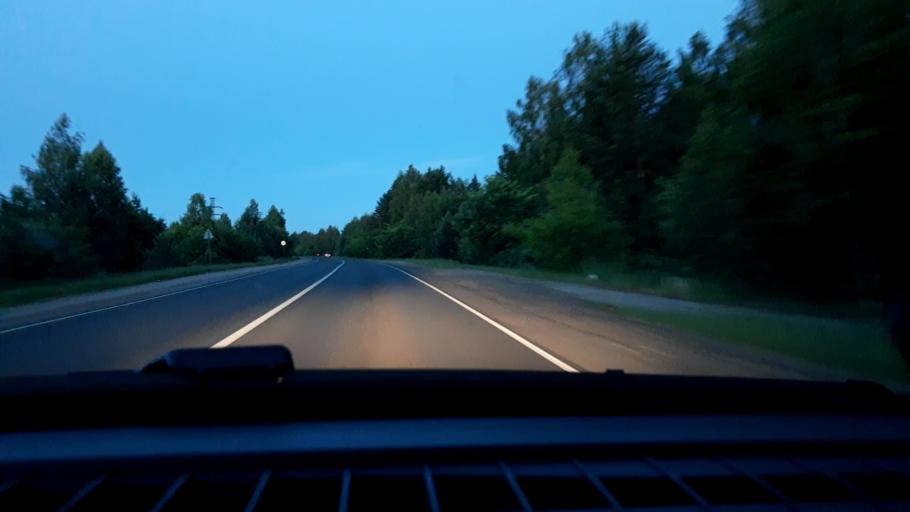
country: RU
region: Nizjnij Novgorod
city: Gidrotorf
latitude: 56.5596
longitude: 43.4975
